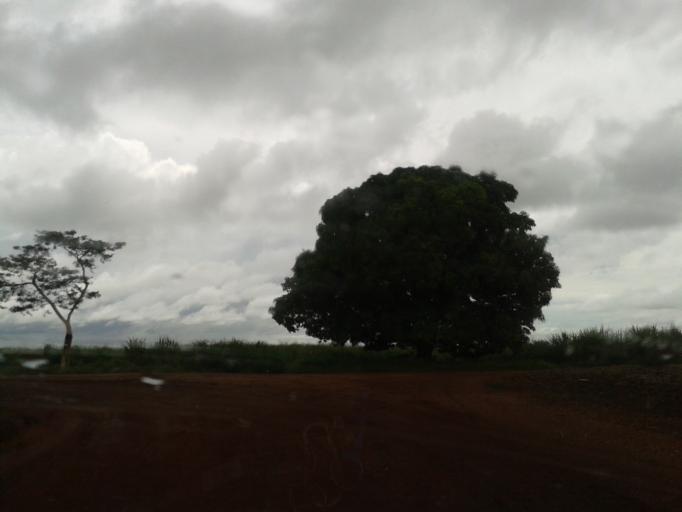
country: BR
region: Minas Gerais
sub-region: Santa Vitoria
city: Santa Vitoria
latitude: -18.6594
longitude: -49.9112
